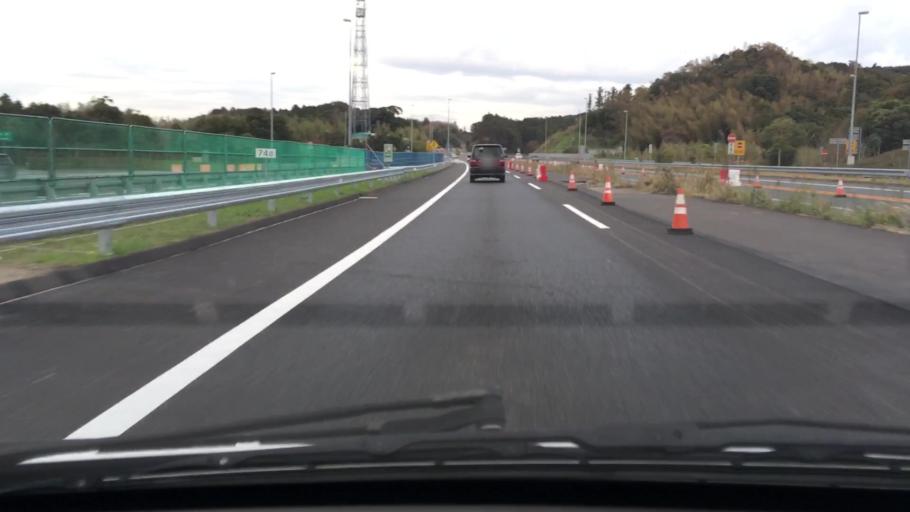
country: JP
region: Chiba
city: Kimitsu
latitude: 35.2828
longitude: 139.9262
